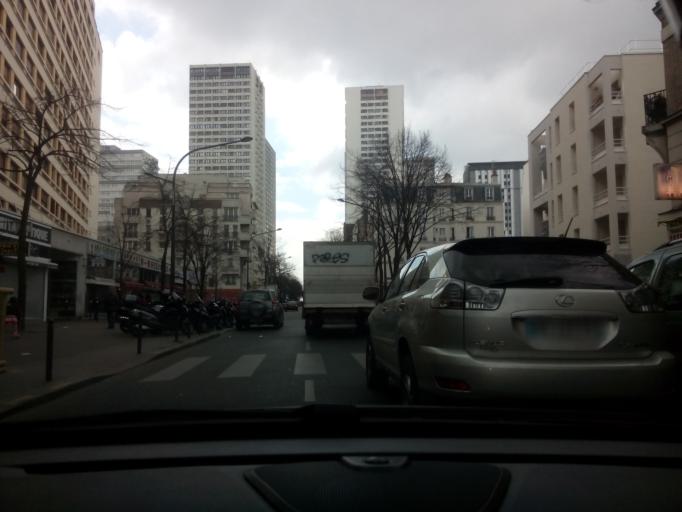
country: FR
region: Ile-de-France
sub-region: Departement du Val-de-Marne
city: Le Kremlin-Bicetre
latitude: 48.8232
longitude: 2.3622
